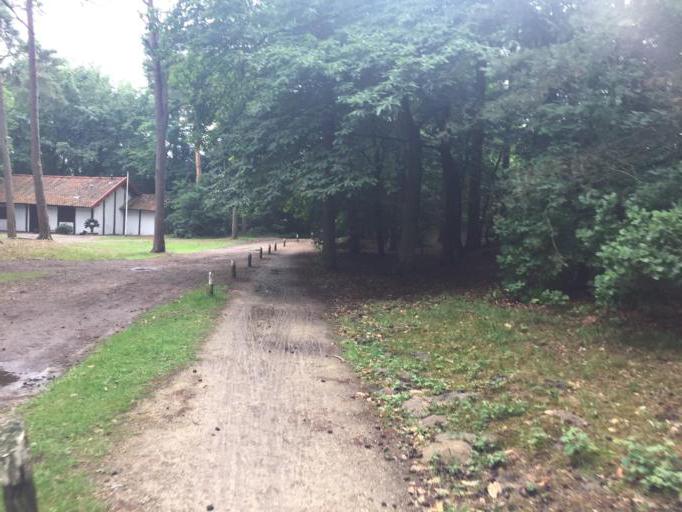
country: NL
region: Utrecht
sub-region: Gemeente Zeist
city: Zeist
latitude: 52.0833
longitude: 5.2644
